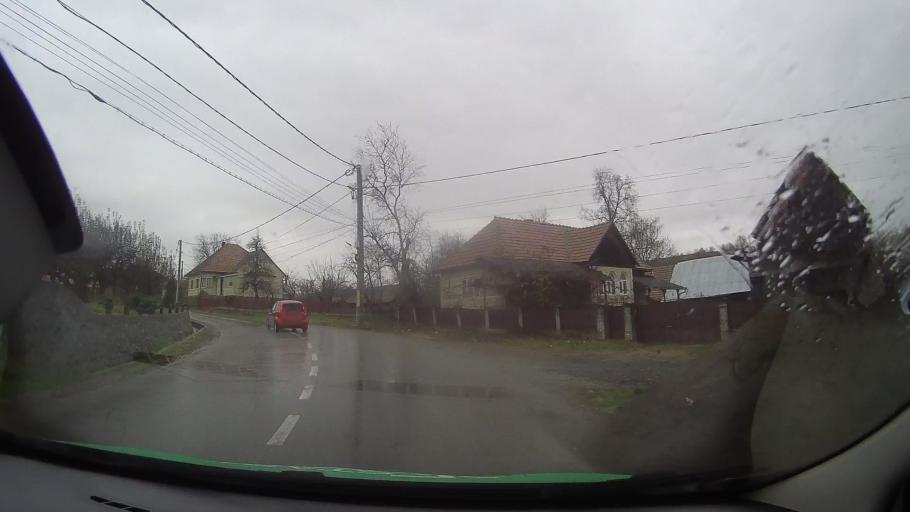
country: RO
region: Mures
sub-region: Comuna Vatava
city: Vatava
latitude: 46.9407
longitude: 24.7662
